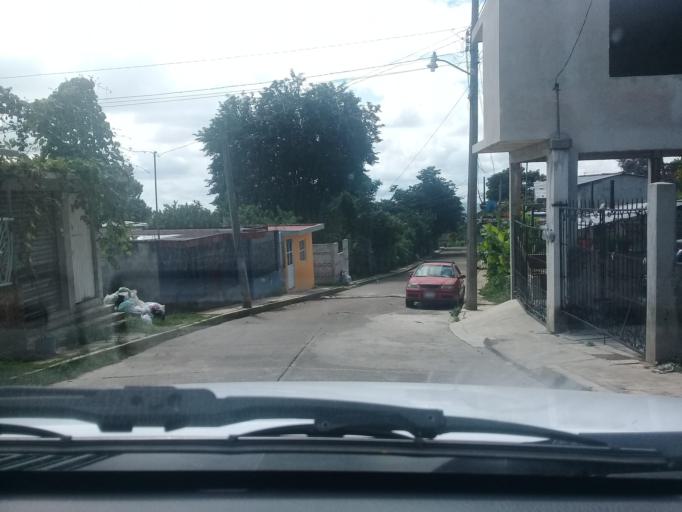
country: MX
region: Veracruz
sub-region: Tlalnelhuayocan
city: Otilpan
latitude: 19.5605
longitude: -96.9793
